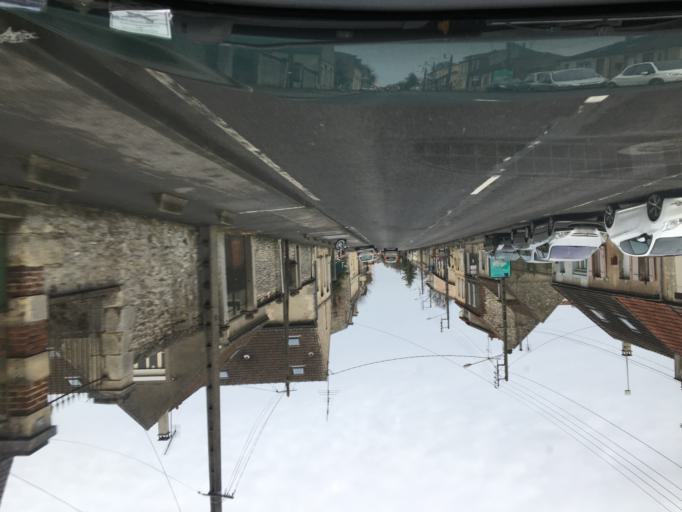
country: FR
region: Picardie
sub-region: Departement de l'Oise
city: Senlis
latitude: 49.1978
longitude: 2.5785
